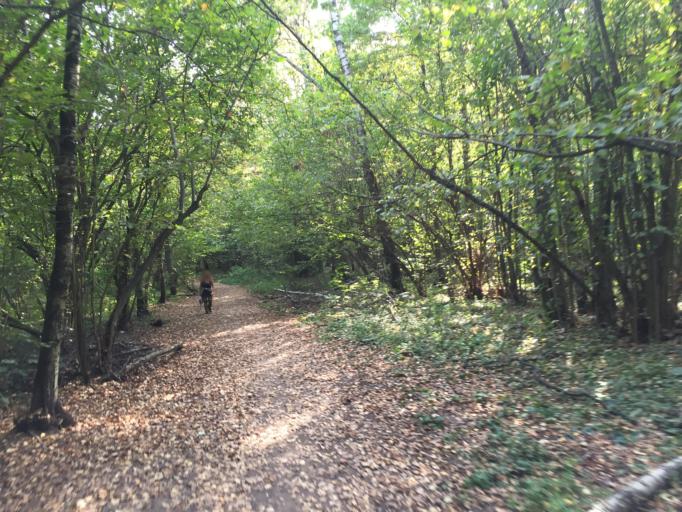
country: RU
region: Moscow
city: Babushkin
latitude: 55.8680
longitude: 37.7298
